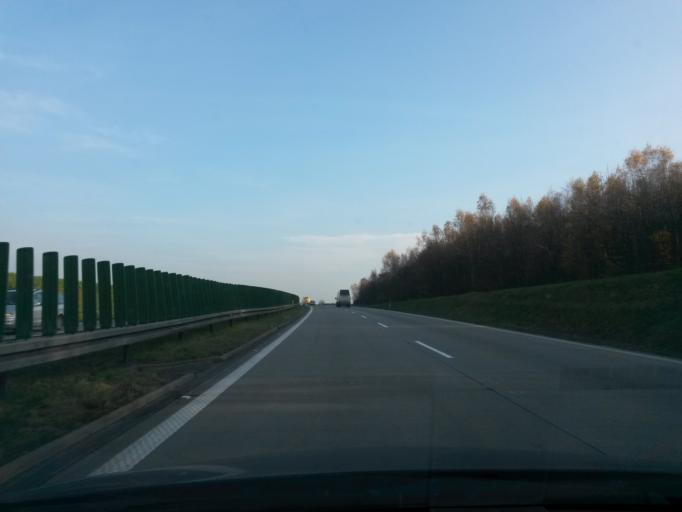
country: PL
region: Lower Silesian Voivodeship
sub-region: Powiat wroclawski
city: Katy Wroclawskie
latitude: 51.0205
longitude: 16.6873
